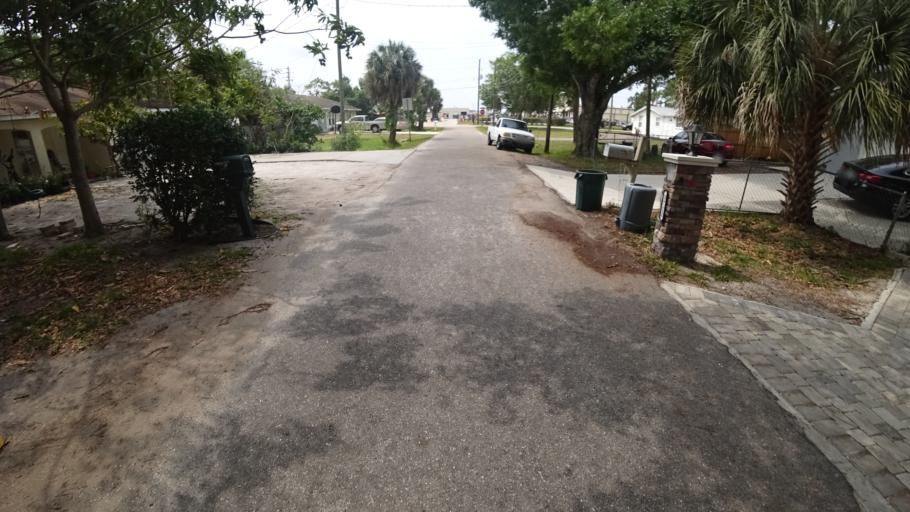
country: US
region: Florida
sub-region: Manatee County
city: Samoset
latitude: 27.4664
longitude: -82.5433
